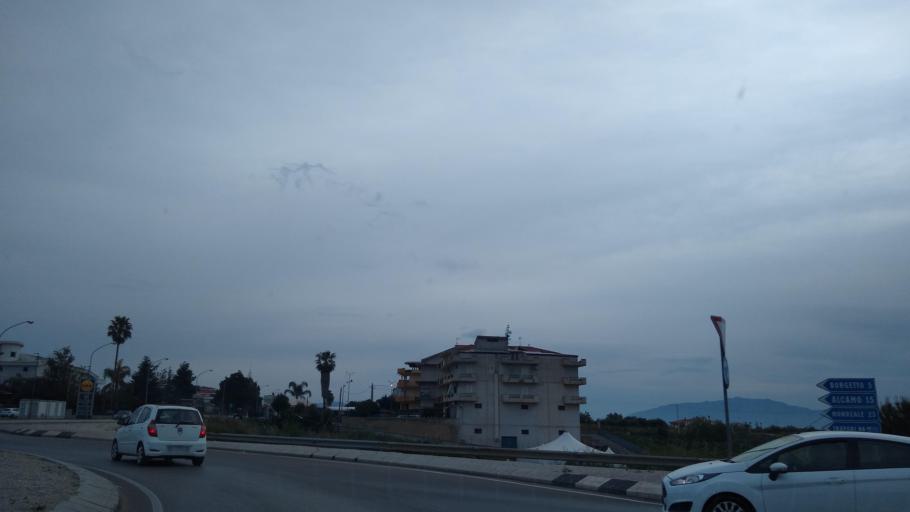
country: IT
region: Sicily
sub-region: Palermo
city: Partinico
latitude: 38.0400
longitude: 13.1077
